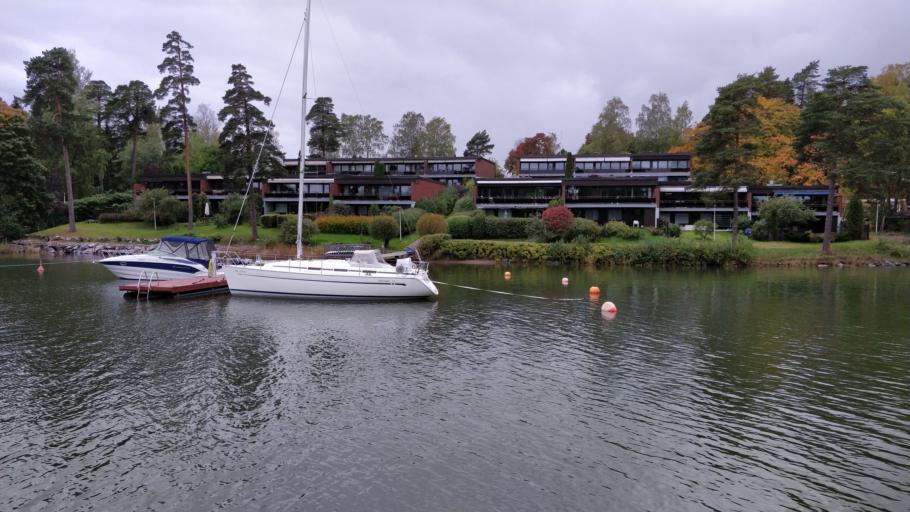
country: FI
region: Uusimaa
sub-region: Helsinki
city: Vantaa
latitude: 60.1850
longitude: 25.0639
